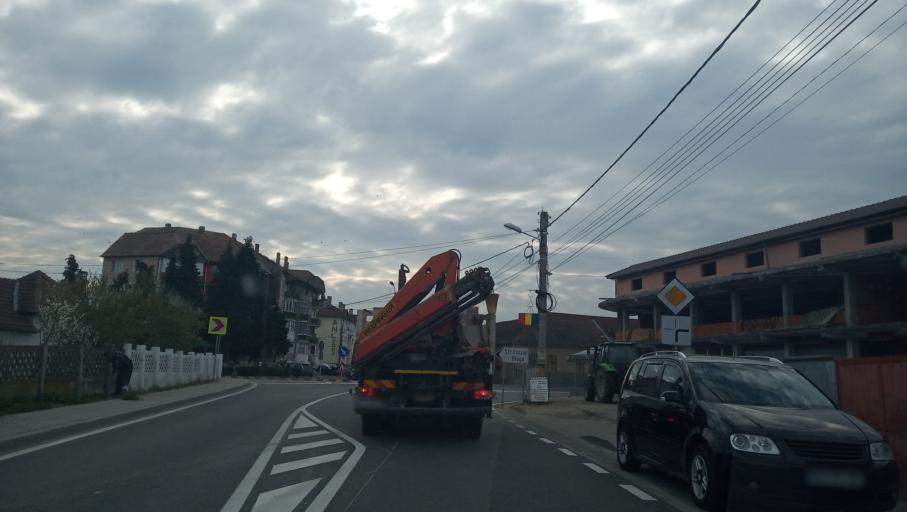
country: RO
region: Bihor
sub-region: Comuna Lunca
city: Lunca
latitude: 46.5379
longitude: 22.4606
